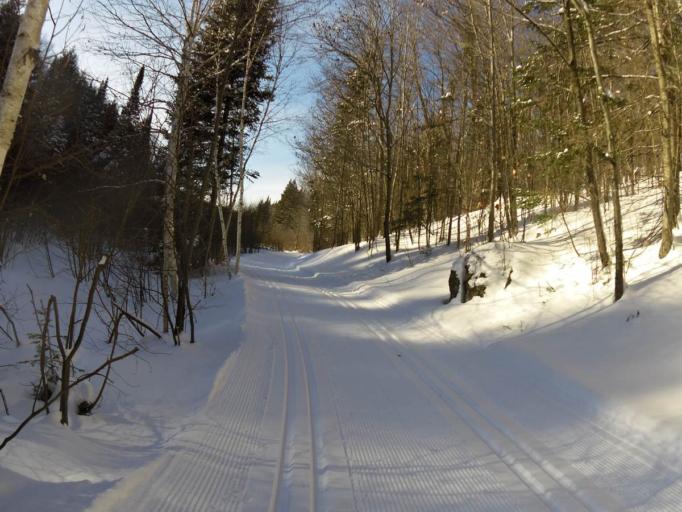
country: CA
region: Quebec
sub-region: Outaouais
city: Wakefield
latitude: 45.6237
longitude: -75.9957
